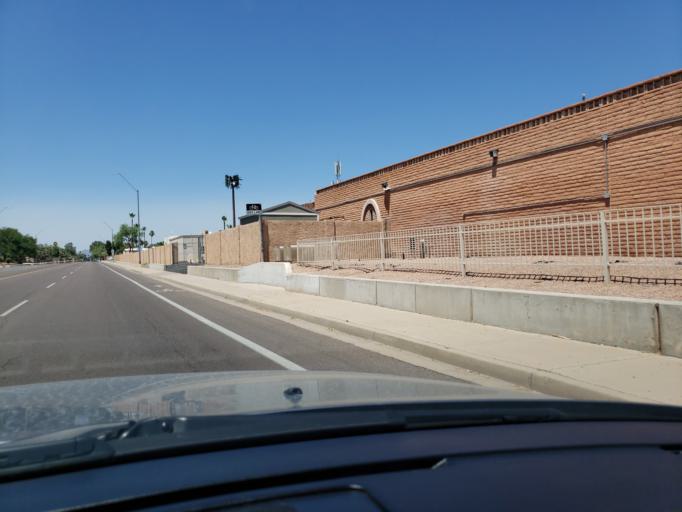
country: US
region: Arizona
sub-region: Maricopa County
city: Paradise Valley
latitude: 33.6043
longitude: -111.9433
